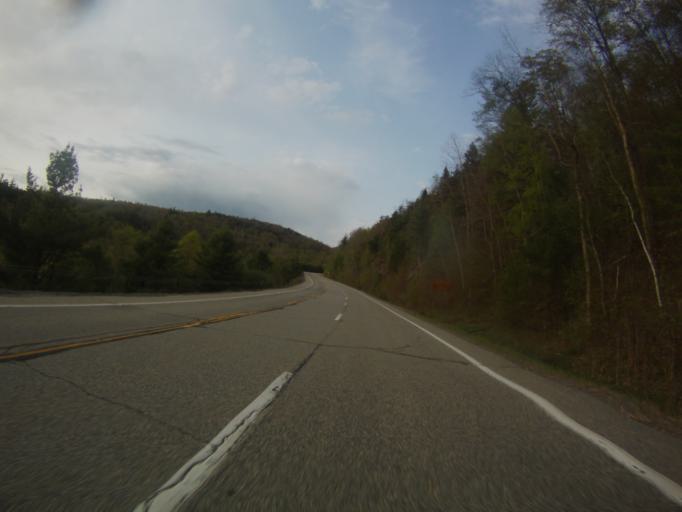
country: US
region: New York
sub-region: Essex County
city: Ticonderoga
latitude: 43.7384
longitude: -73.5943
